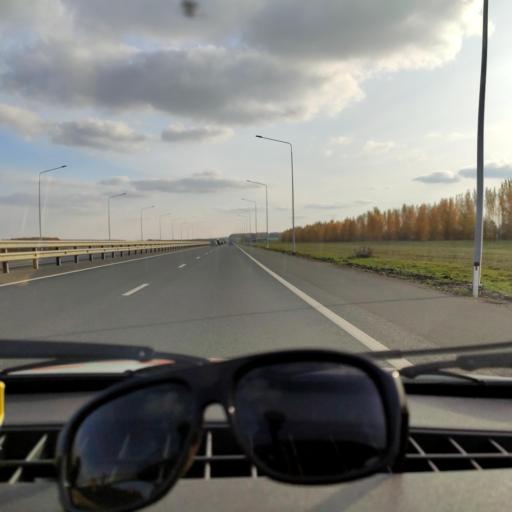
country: RU
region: Bashkortostan
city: Tolbazy
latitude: 54.1656
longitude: 55.9024
